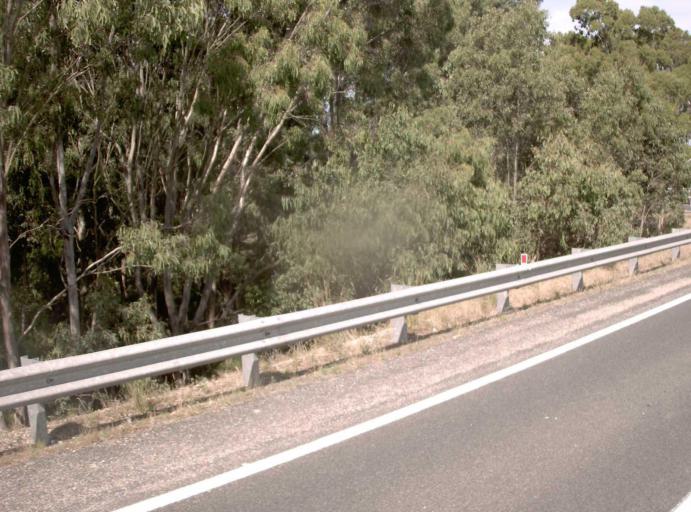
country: AU
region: Victoria
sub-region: East Gippsland
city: Bairnsdale
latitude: -37.8171
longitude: 147.7576
